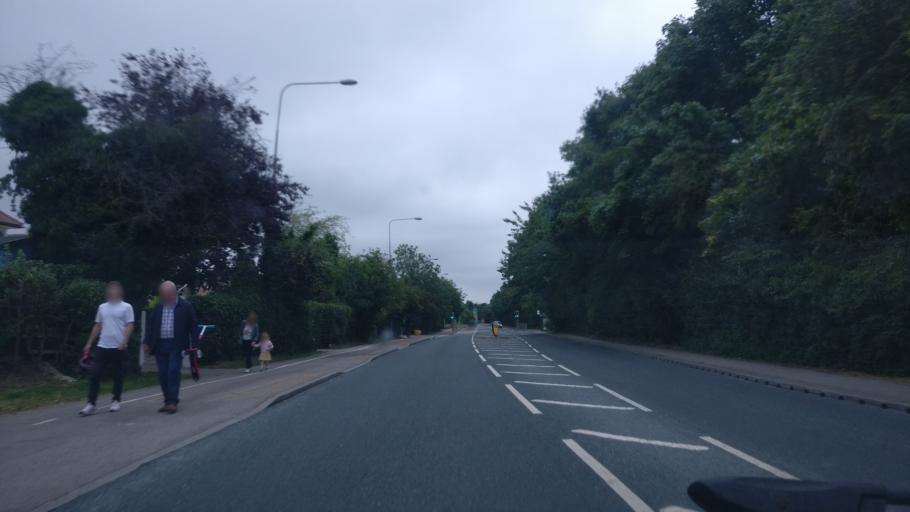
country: GB
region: England
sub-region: East Riding of Yorkshire
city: Beverley
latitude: 53.8295
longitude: -0.4387
